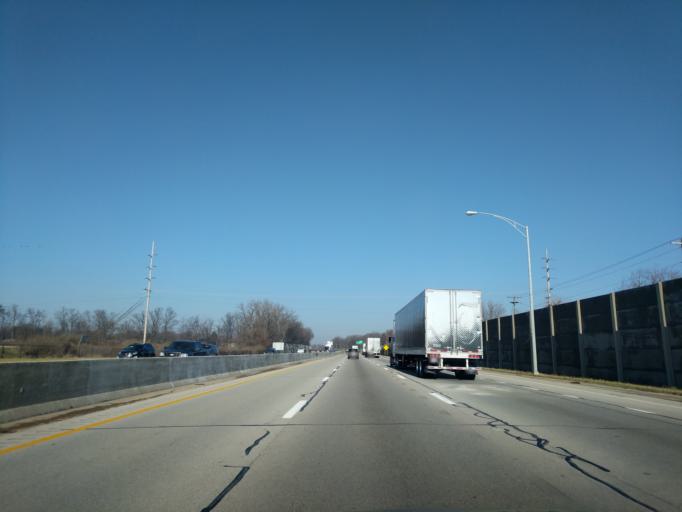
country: US
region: Ohio
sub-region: Miami County
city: Tipp City
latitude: 39.9664
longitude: -84.1895
